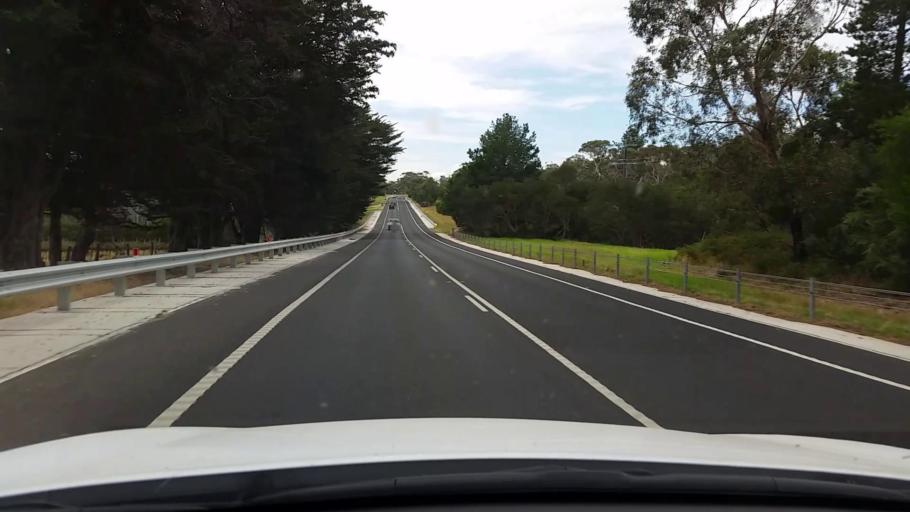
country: AU
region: Victoria
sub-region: Mornington Peninsula
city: Safety Beach
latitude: -38.3202
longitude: 145.0151
